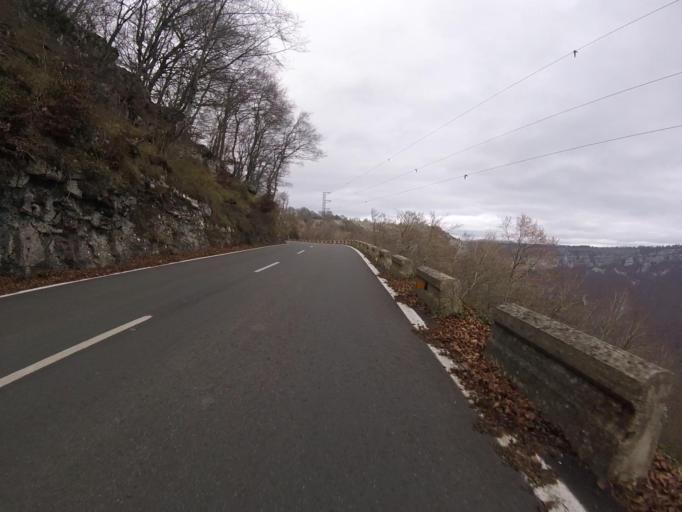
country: ES
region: Navarre
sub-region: Provincia de Navarra
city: Eulate
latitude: 42.7946
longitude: -2.1407
